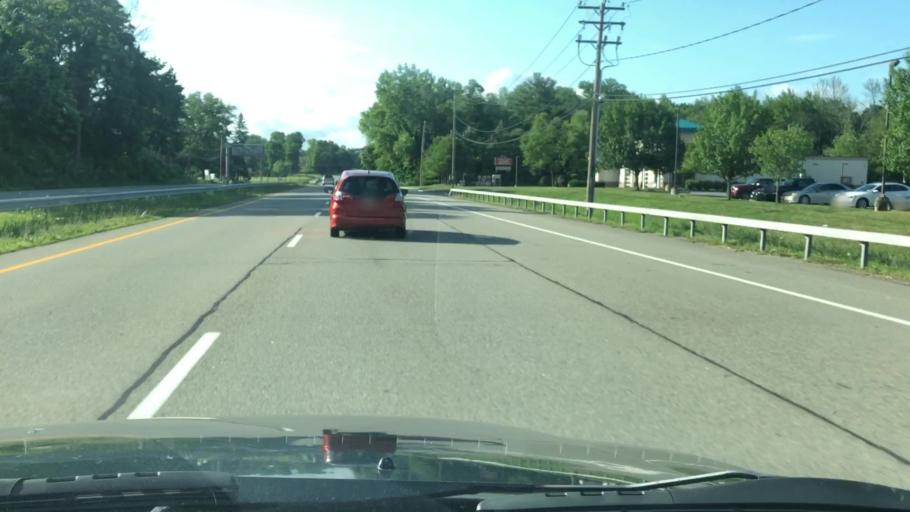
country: US
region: New York
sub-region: Dutchess County
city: Fishkill
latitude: 41.5395
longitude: -73.9010
